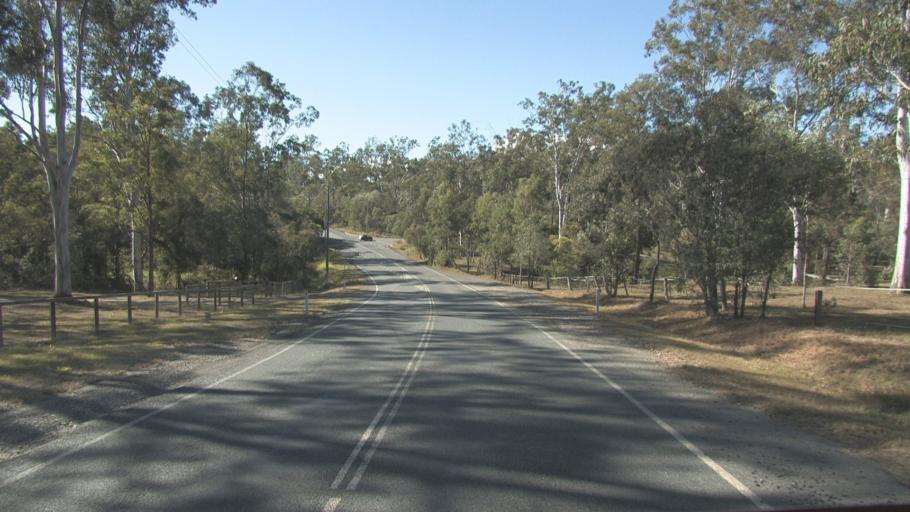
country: AU
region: Queensland
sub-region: Logan
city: Cedar Vale
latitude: -27.8344
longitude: 153.0519
